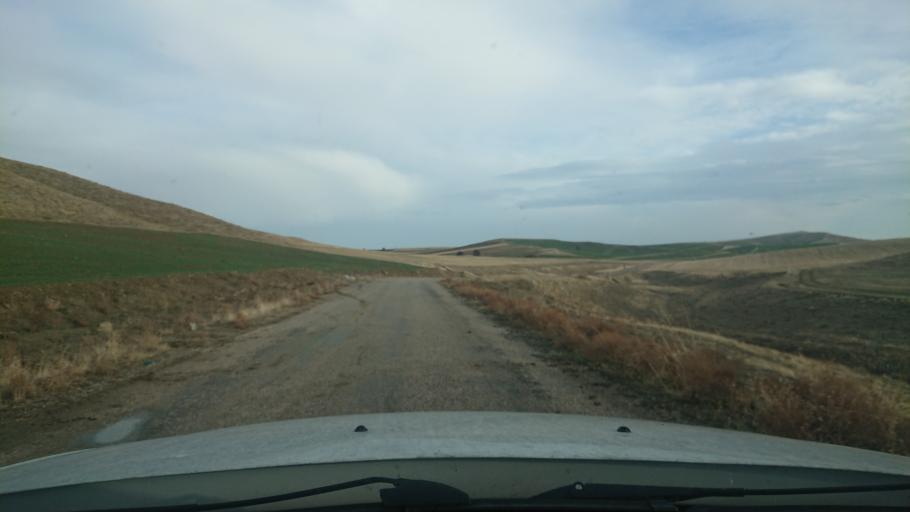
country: TR
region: Aksaray
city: Acipinar
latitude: 38.6416
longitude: 33.8082
